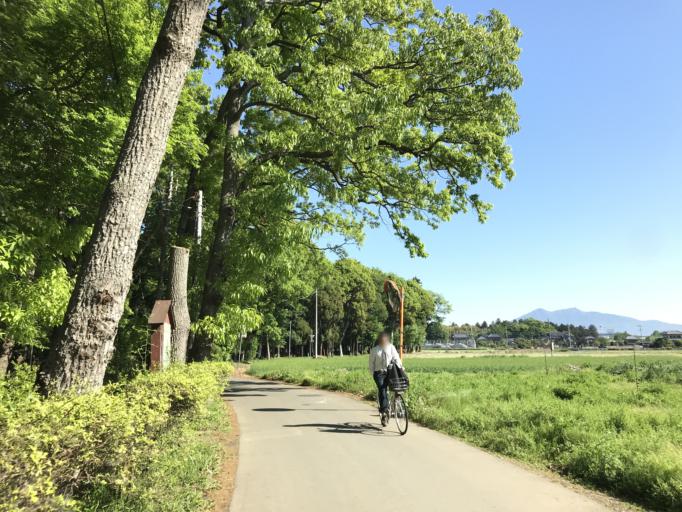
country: JP
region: Ibaraki
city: Tsukuba
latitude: 36.1078
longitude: 140.0669
